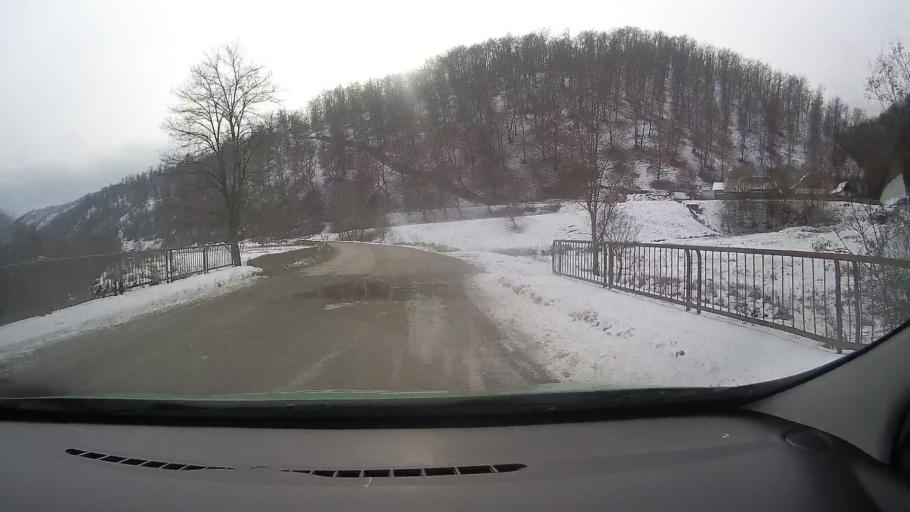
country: RO
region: Alba
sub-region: Oras Zlatna
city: Zlatna
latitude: 46.1189
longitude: 23.2056
